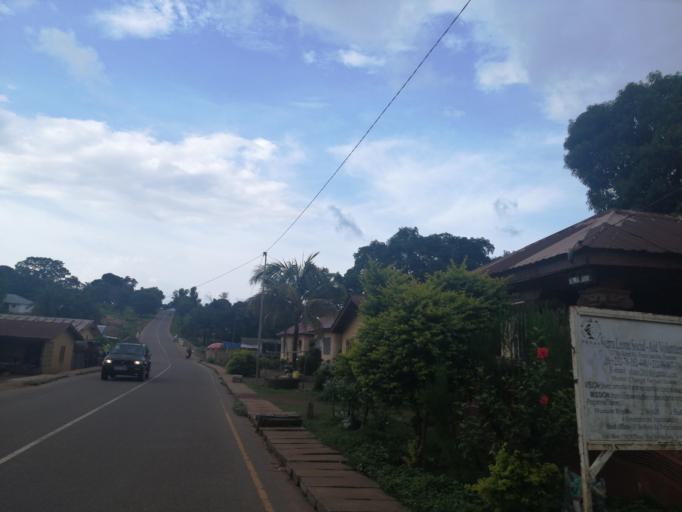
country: SL
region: Northern Province
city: Port Loko
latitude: 8.7697
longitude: -12.7866
